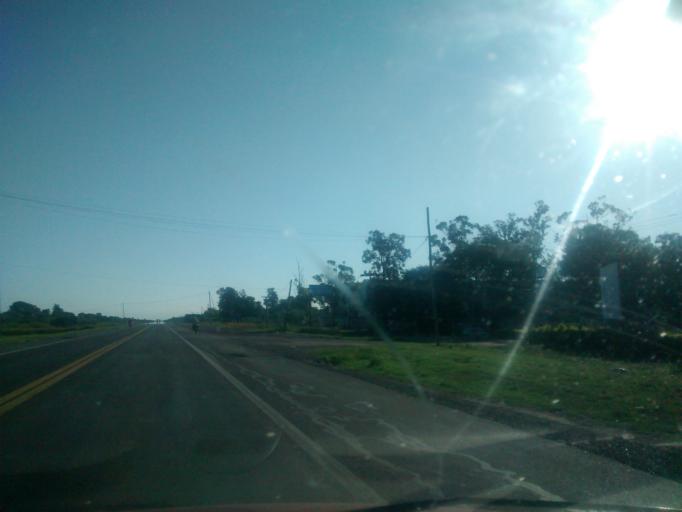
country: AR
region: Chaco
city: Fontana
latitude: -27.4683
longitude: -59.0483
